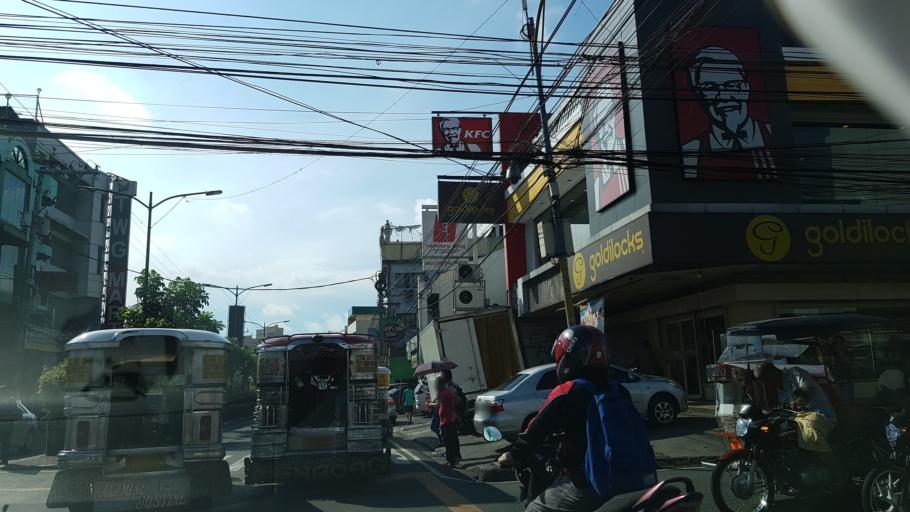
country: PH
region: Metro Manila
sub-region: Mandaluyong
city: Mandaluyong City
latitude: 14.5759
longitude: 121.0410
